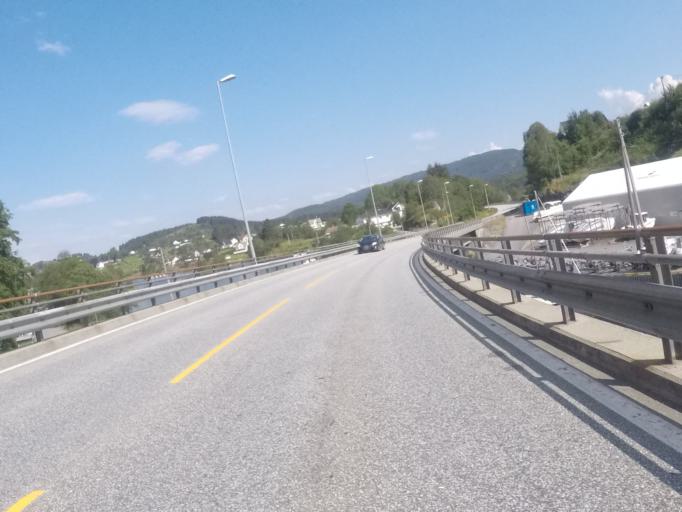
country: NO
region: Hordaland
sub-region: Bergen
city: Hylkje
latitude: 60.6032
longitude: 5.3968
